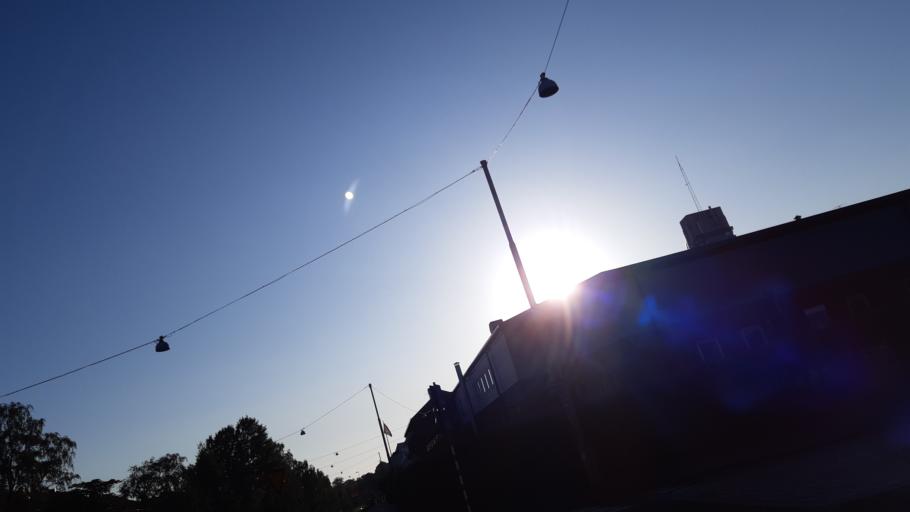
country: SE
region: Vaestra Goetaland
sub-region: Goteborg
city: Eriksbo
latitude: 57.7180
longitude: 12.0318
